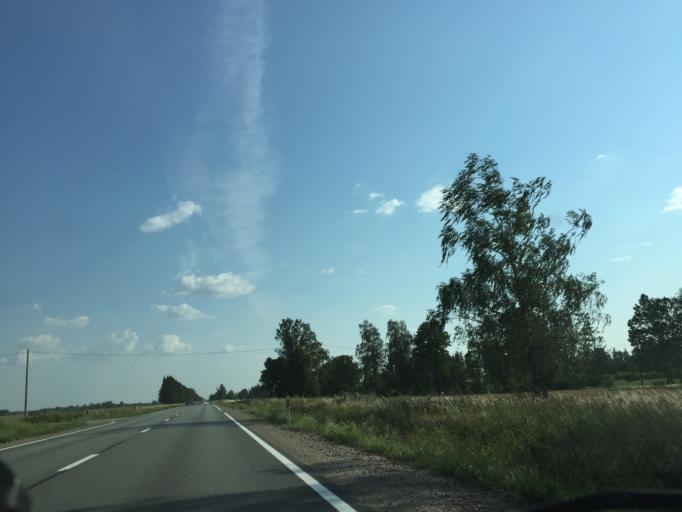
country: LV
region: Jelgava
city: Jelgava
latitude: 56.4729
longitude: 23.6946
